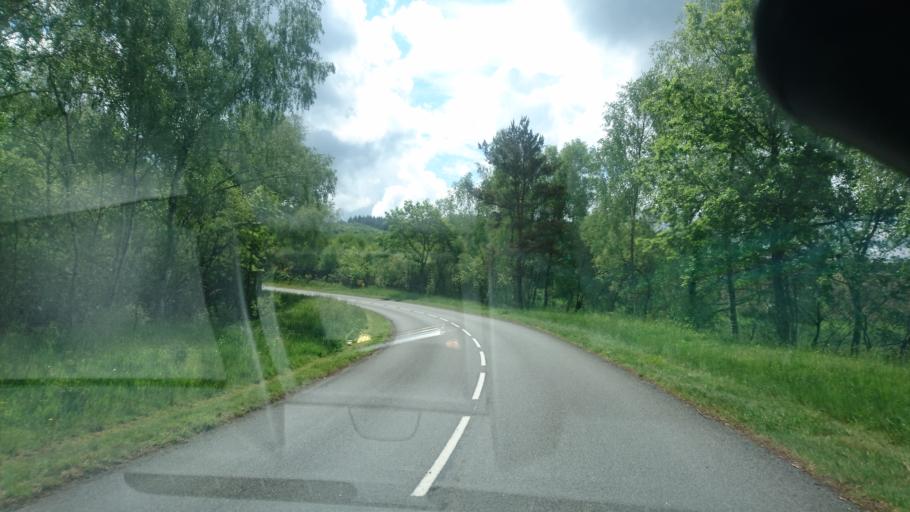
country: FR
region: Limousin
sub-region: Departement de la Haute-Vienne
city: Peyrat-le-Chateau
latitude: 45.7775
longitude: 1.8638
